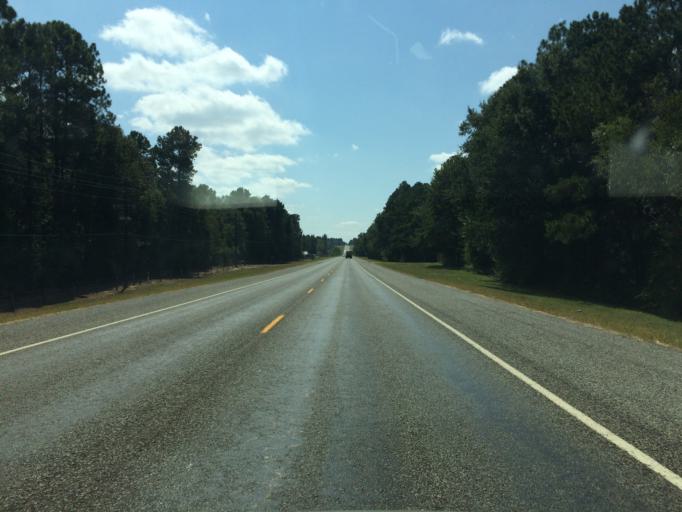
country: US
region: Texas
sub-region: Wood County
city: Hawkins
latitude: 32.7097
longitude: -95.2045
